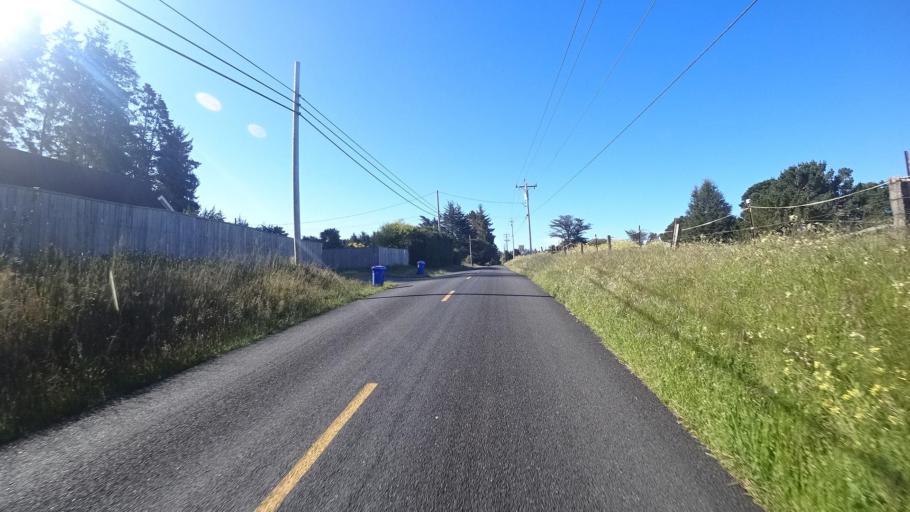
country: US
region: California
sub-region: Humboldt County
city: McKinleyville
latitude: 40.9922
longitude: -124.1005
